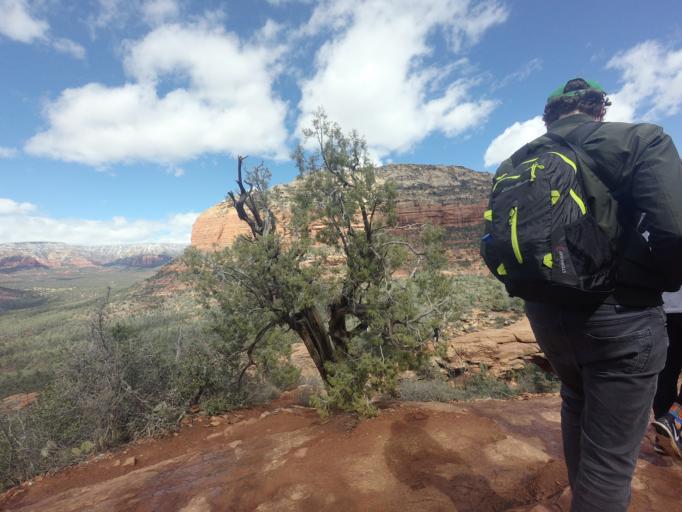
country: US
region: Arizona
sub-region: Yavapai County
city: West Sedona
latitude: 34.8974
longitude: -111.8079
